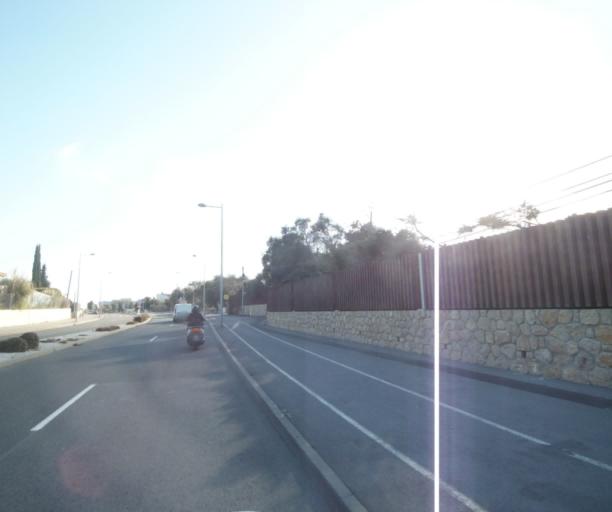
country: FR
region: Provence-Alpes-Cote d'Azur
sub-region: Departement des Alpes-Maritimes
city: Biot
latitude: 43.5996
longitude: 7.1130
